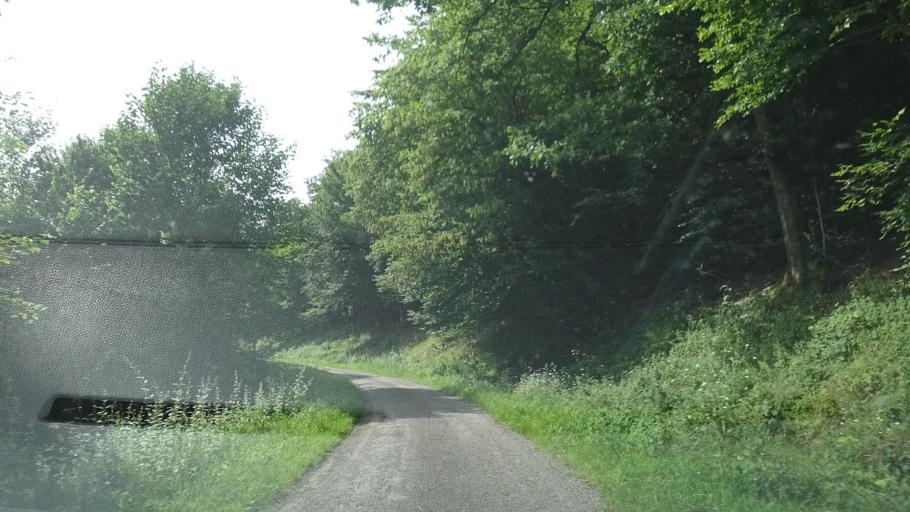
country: BE
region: Wallonia
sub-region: Province du Luxembourg
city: Herbeumont
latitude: 49.7814
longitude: 5.2585
